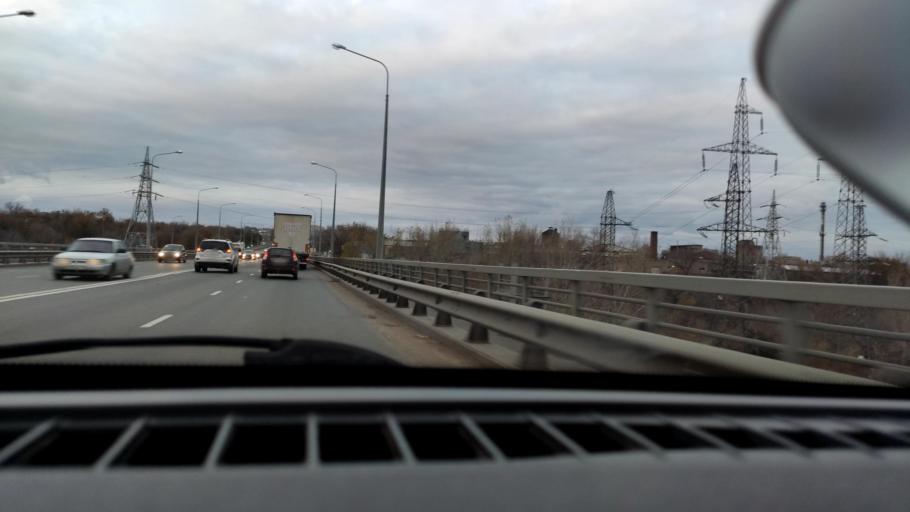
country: RU
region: Samara
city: Samara
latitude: 53.1702
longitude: 50.1954
